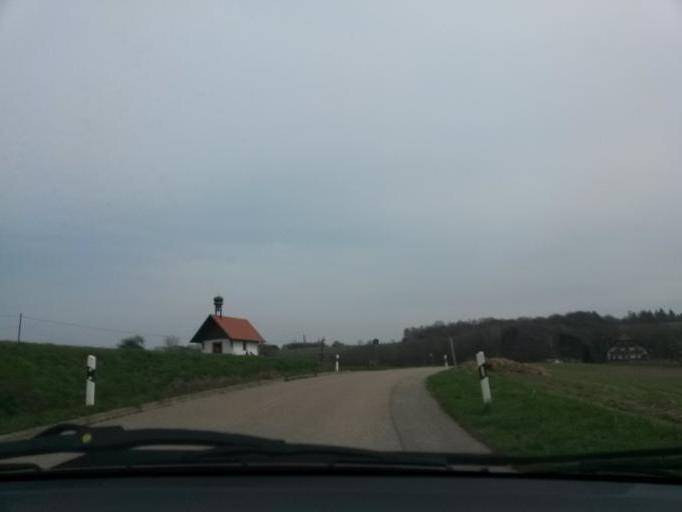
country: DE
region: Baden-Wuerttemberg
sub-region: Freiburg Region
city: Hohberg
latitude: 48.3104
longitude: 7.8941
